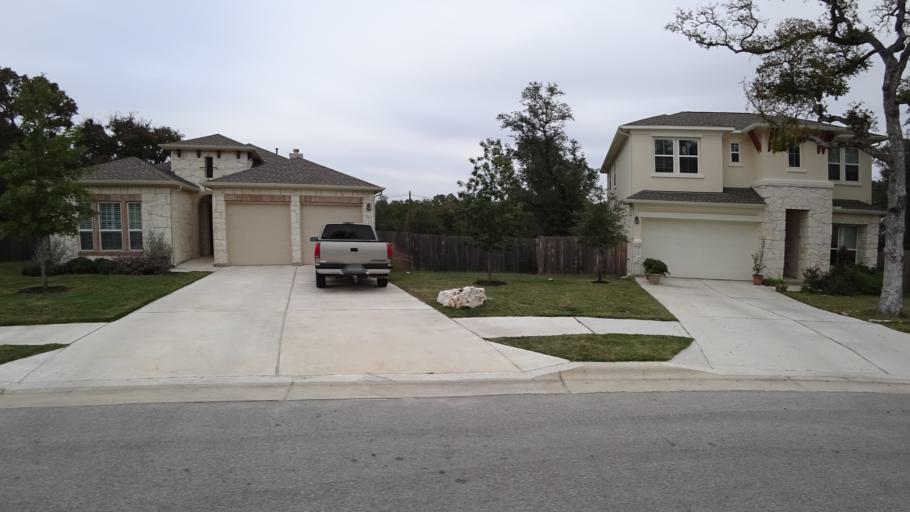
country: US
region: Texas
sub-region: Travis County
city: Shady Hollow
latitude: 30.1847
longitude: -97.8993
